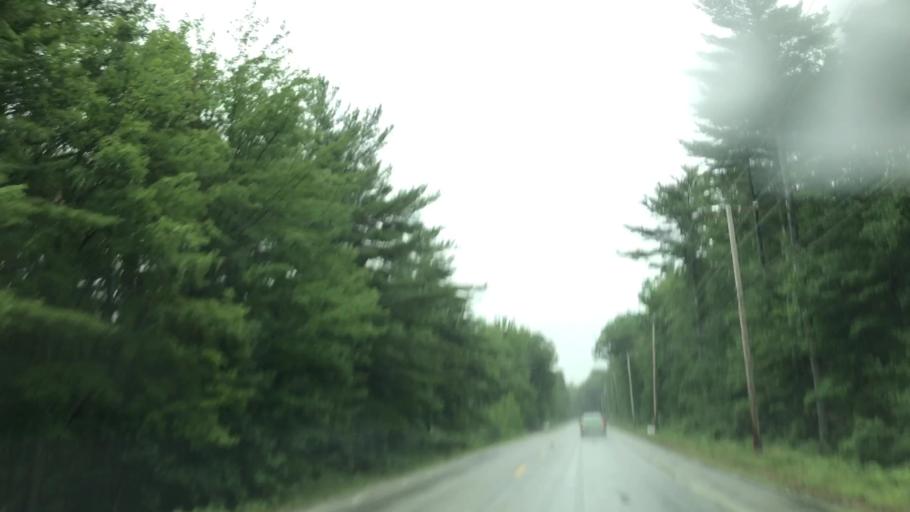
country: US
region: Maine
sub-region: York County
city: South Berwick
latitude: 43.2846
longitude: -70.8045
